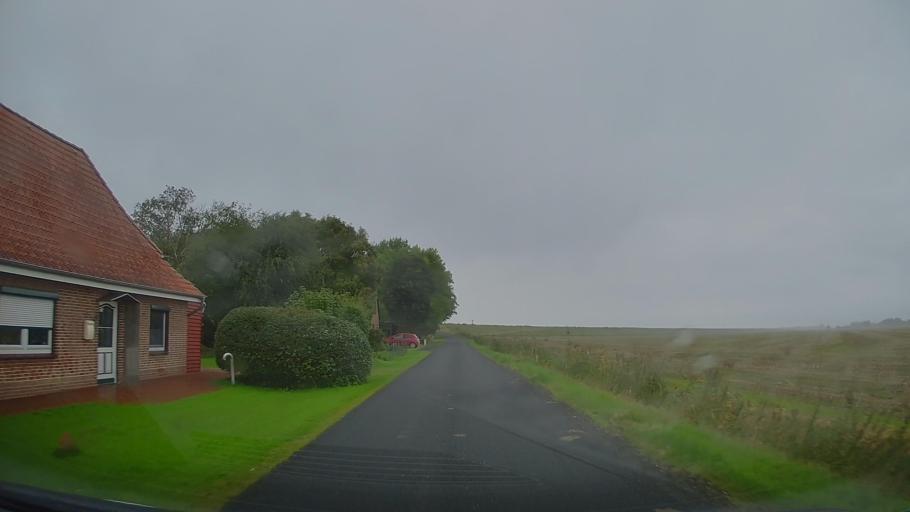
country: DE
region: Schleswig-Holstein
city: Elpersbuttel
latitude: 54.0953
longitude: 9.0072
